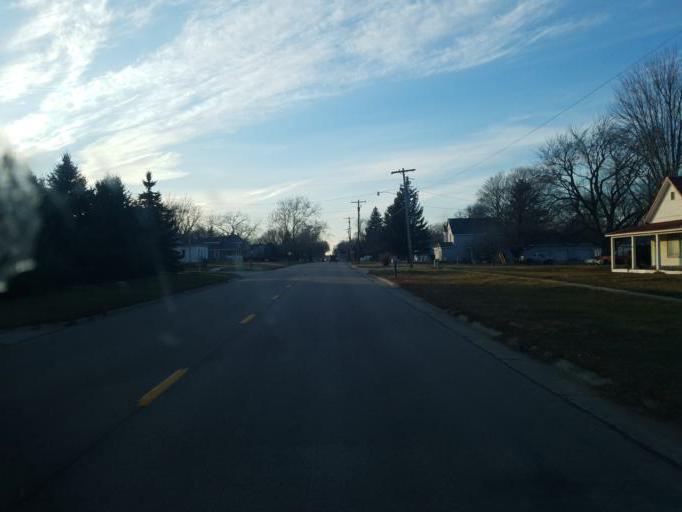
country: US
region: South Dakota
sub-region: Yankton County
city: Yankton
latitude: 42.7288
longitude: -97.4924
